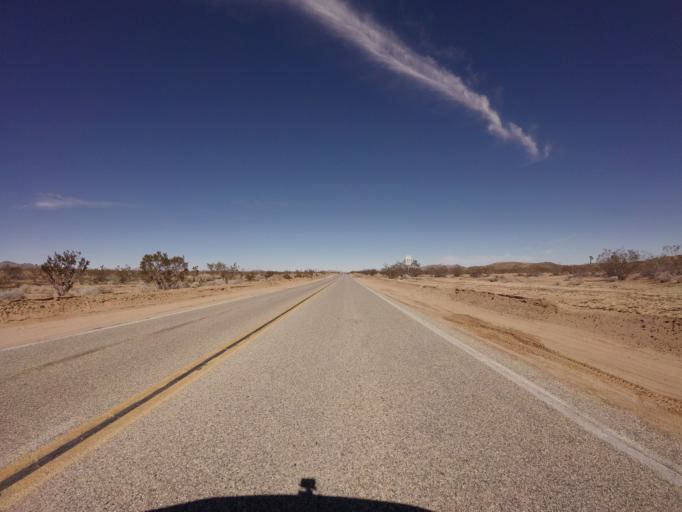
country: US
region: California
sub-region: San Bernardino County
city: Yucca Valley
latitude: 34.2378
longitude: -116.3934
